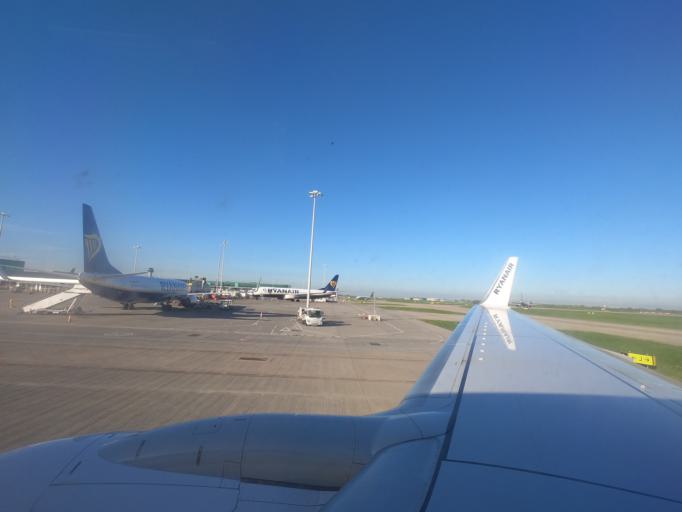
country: GB
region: England
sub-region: Essex
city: Takeley
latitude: 51.8945
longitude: 0.2585
